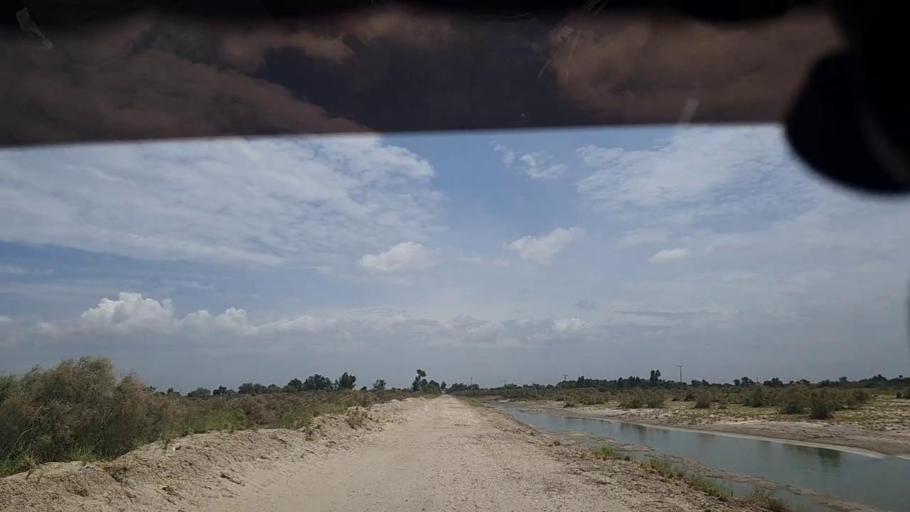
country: PK
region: Sindh
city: Rustam jo Goth
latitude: 28.0277
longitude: 68.9368
